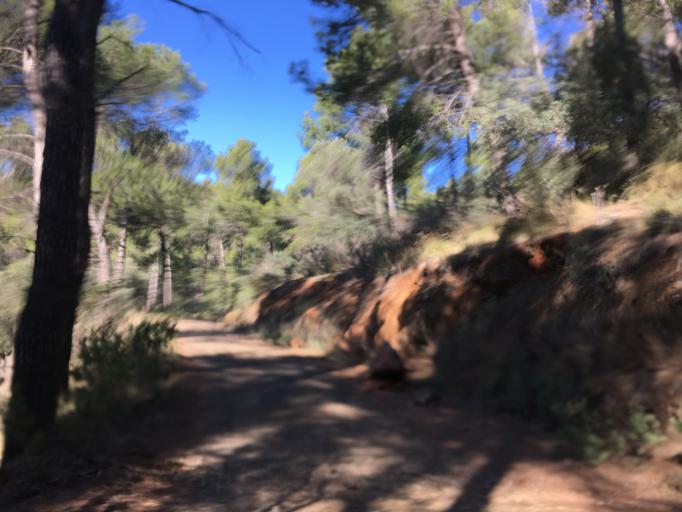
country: ES
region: Andalusia
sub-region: Provincia de Malaga
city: Malaga
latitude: 36.8023
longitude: -4.3991
